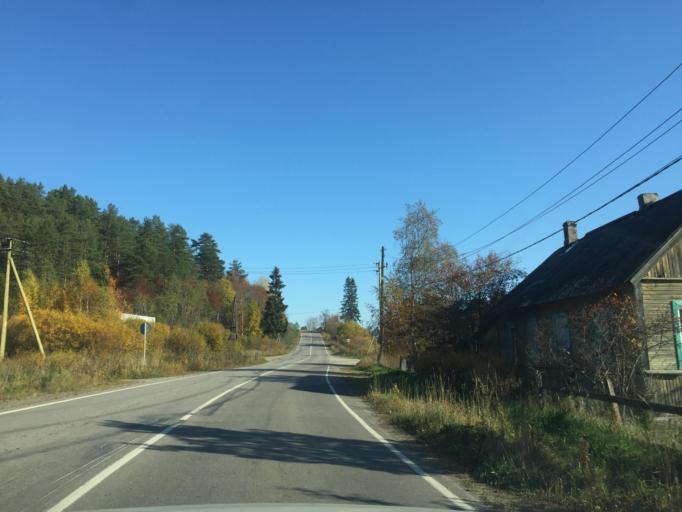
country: RU
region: Leningrad
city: Kuznechnoye
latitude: 61.3015
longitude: 29.9135
